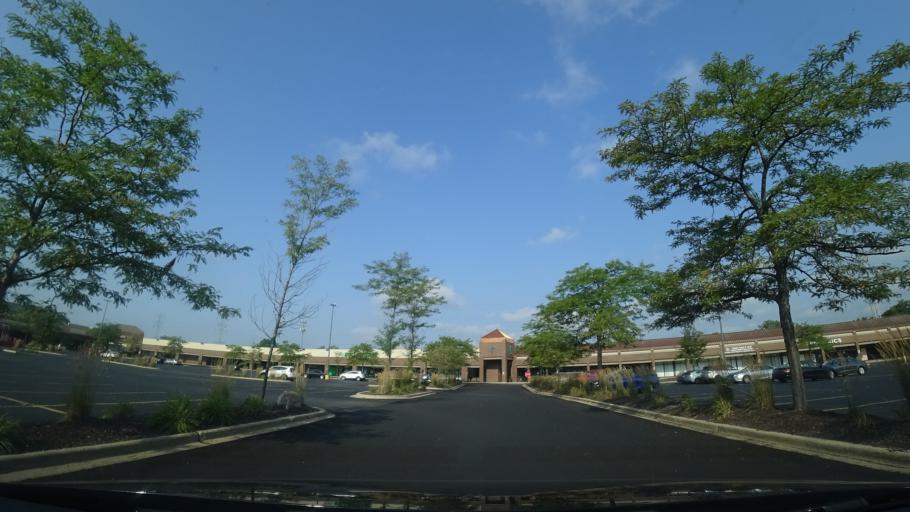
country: US
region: Illinois
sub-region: Cook County
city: Evanston
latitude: 42.0399
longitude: -87.7002
